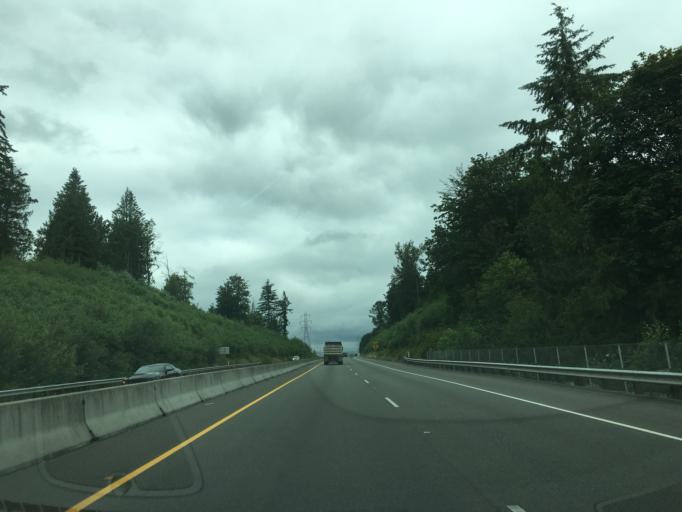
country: US
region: Washington
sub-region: Snohomish County
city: West Lake Stevens
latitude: 48.0162
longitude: -122.1085
